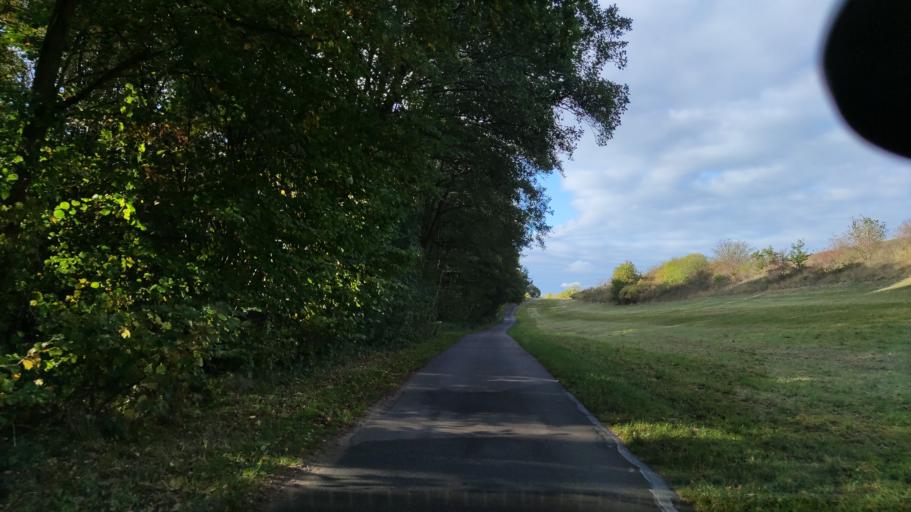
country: DE
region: Lower Saxony
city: Vastorf
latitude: 53.1651
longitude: 10.5313
